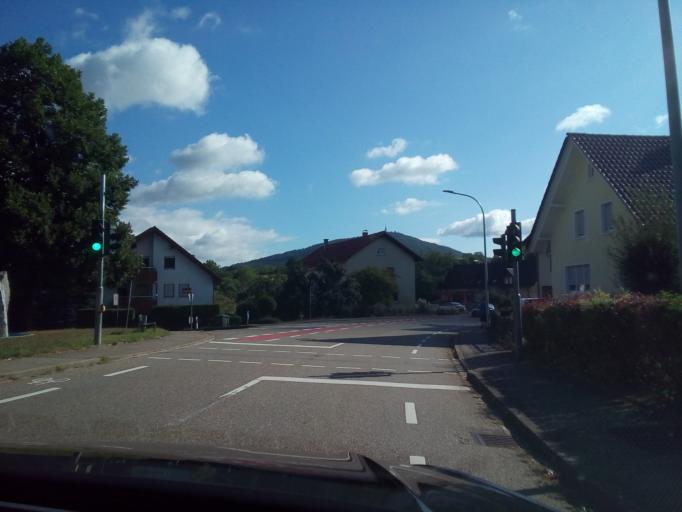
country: DE
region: Baden-Wuerttemberg
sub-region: Karlsruhe Region
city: Sinzheim
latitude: 48.7320
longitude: 8.1645
